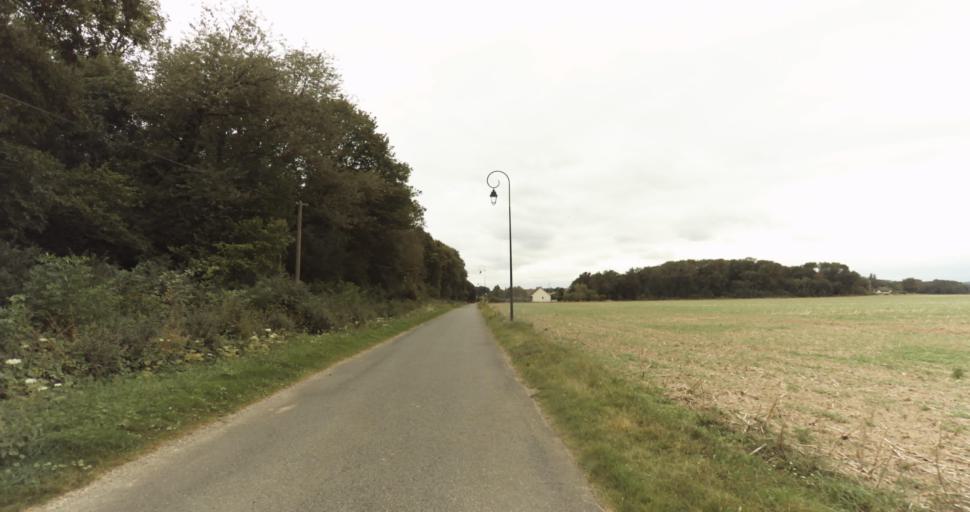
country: FR
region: Haute-Normandie
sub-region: Departement de l'Eure
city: Gravigny
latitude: 49.0304
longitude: 1.2039
